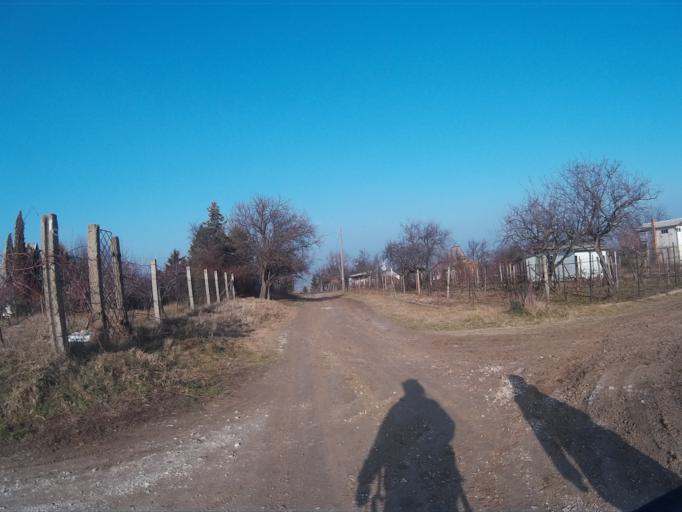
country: HU
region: Komarom-Esztergom
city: Labatlan
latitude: 47.7411
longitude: 18.4824
